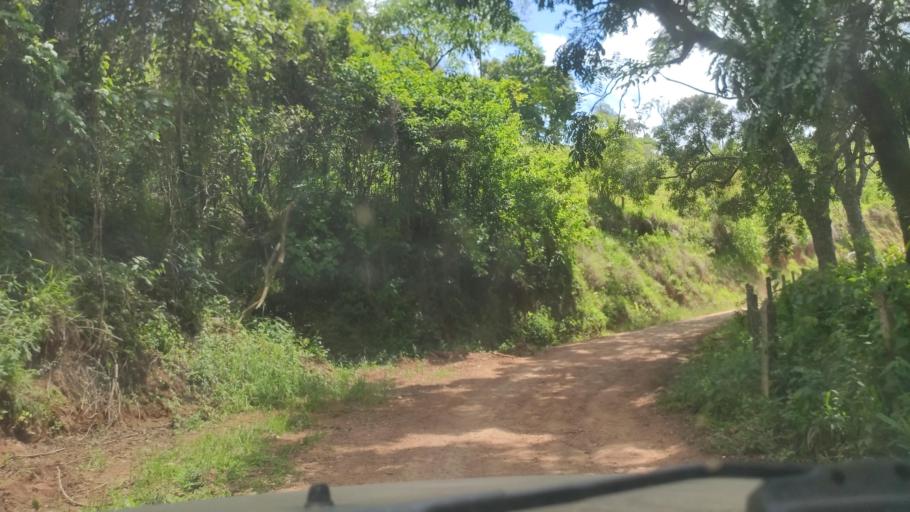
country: BR
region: Minas Gerais
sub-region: Cambui
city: Cambui
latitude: -22.6797
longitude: -45.9698
